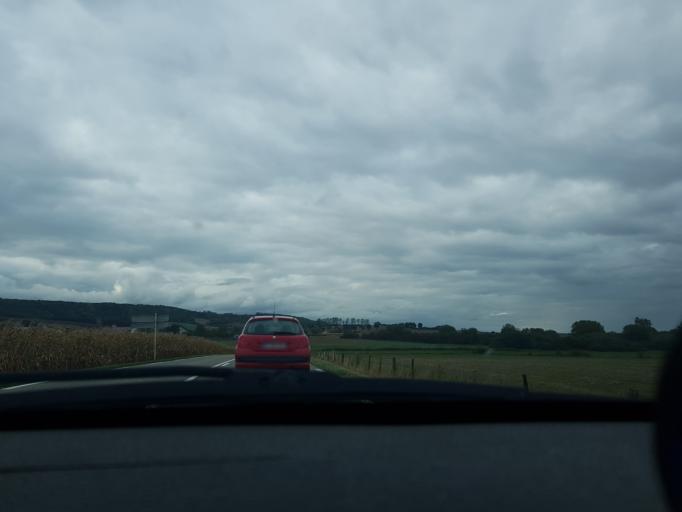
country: FR
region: Lorraine
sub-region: Departement de la Moselle
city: Chateau-Salins
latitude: 48.8297
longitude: 6.5032
